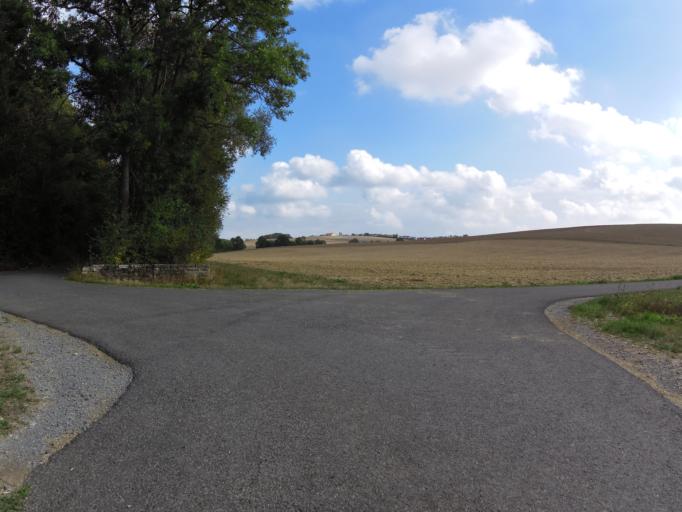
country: DE
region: Bavaria
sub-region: Regierungsbezirk Unterfranken
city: Waldbrunn
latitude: 49.7733
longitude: 9.8119
